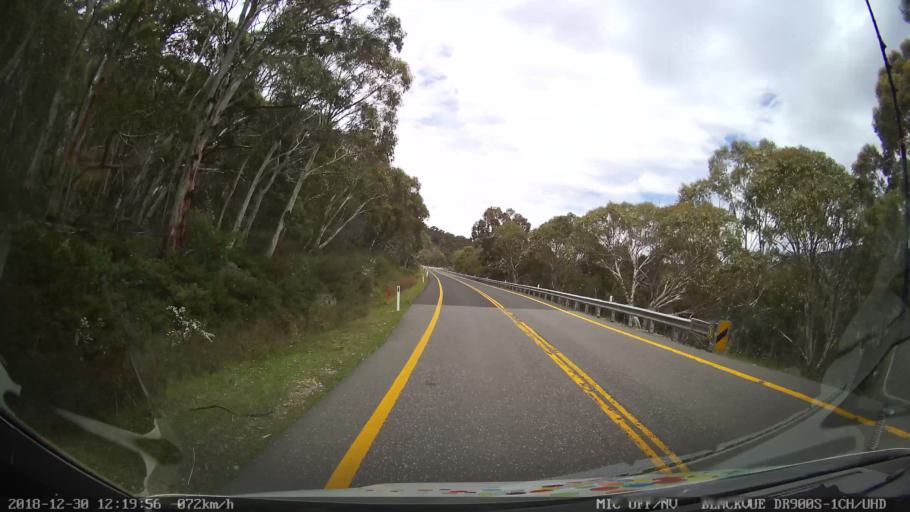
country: AU
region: New South Wales
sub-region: Snowy River
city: Jindabyne
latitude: -36.3448
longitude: 148.5357
